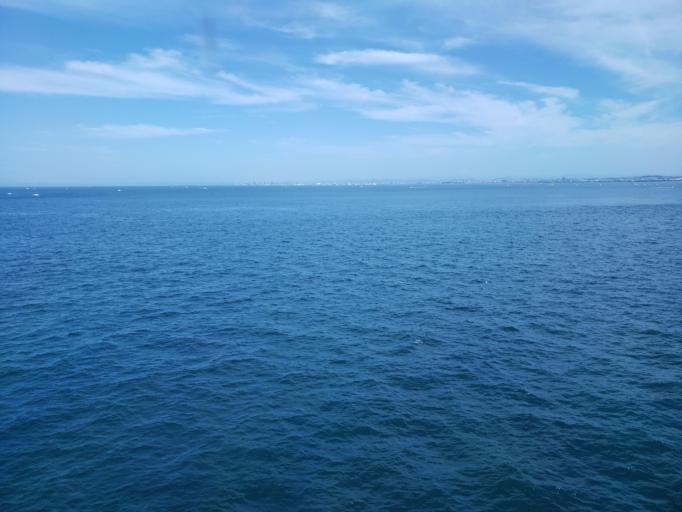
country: JP
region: Hyogo
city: Akashi
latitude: 34.6151
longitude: 134.9374
